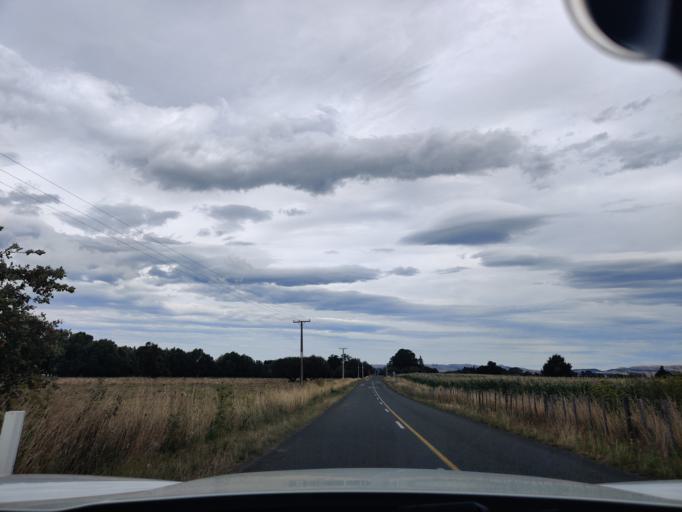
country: NZ
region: Wellington
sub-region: Masterton District
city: Masterton
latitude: -41.0359
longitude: 175.4942
